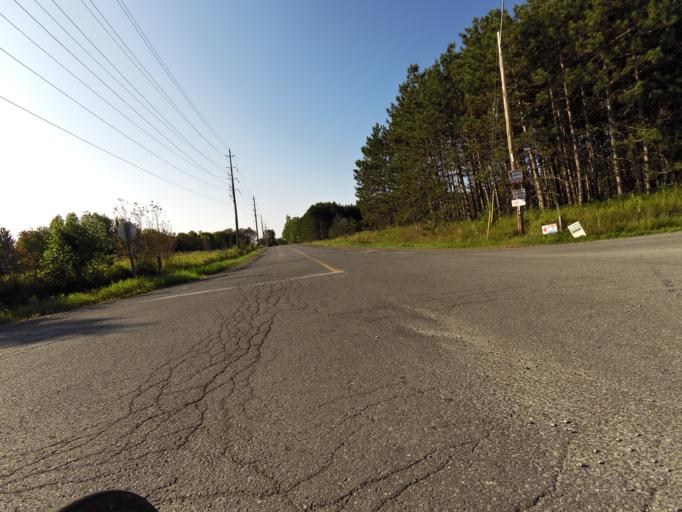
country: CA
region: Ontario
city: Bells Corners
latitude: 45.4592
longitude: -76.0197
